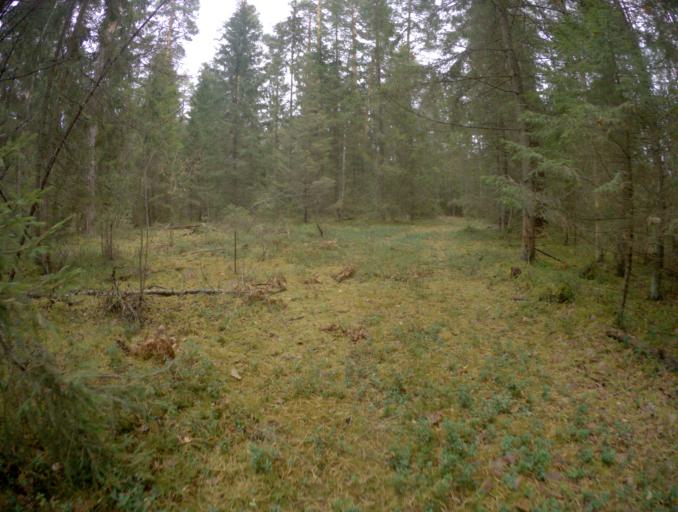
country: RU
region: Vladimir
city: Orgtrud
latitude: 56.1079
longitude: 40.6075
